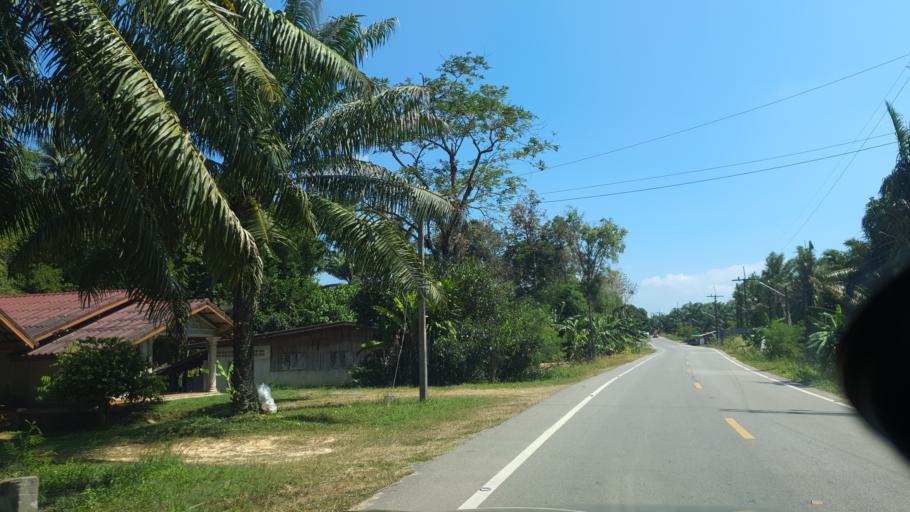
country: TH
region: Krabi
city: Khlong Thom
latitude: 7.9305
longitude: 99.2246
